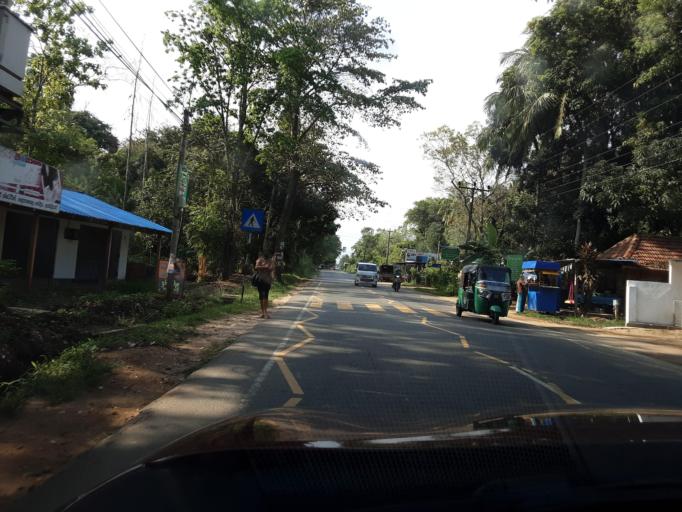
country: LK
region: Uva
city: Haputale
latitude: 6.6570
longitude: 81.1152
